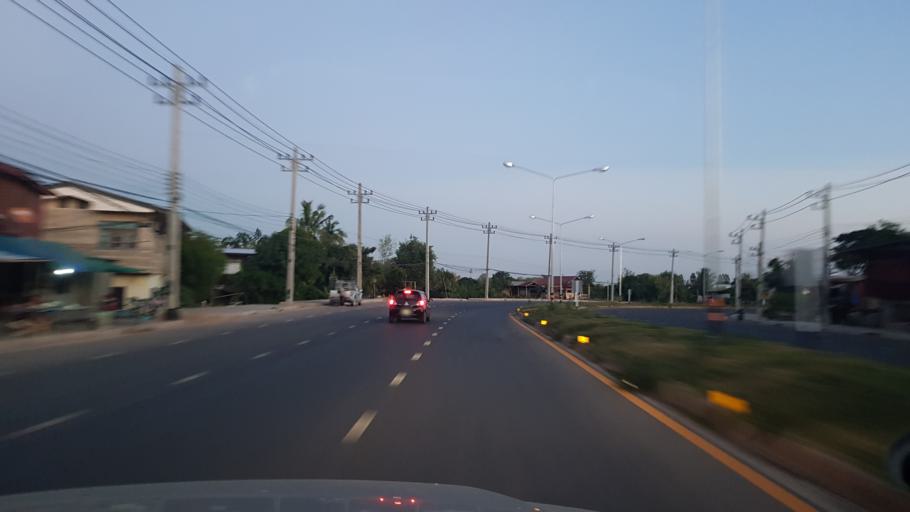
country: TH
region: Chaiyaphum
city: Phu Khiao
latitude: 16.3608
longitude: 102.1480
